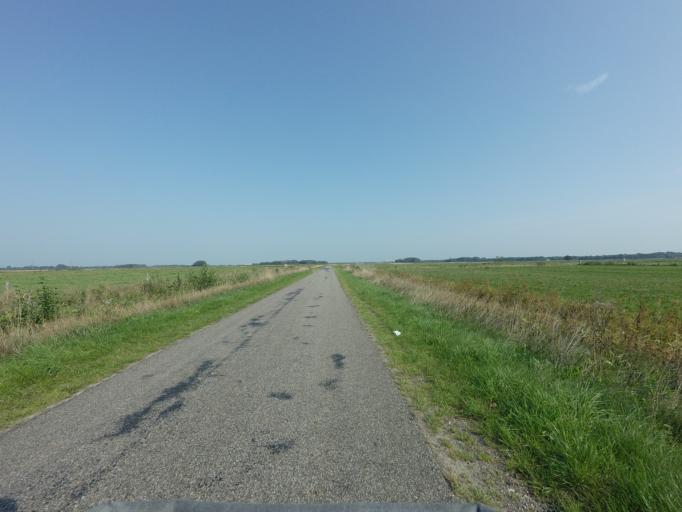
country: NL
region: Drenthe
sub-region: Gemeente Tynaarlo
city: Vries
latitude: 53.1425
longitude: 6.5312
